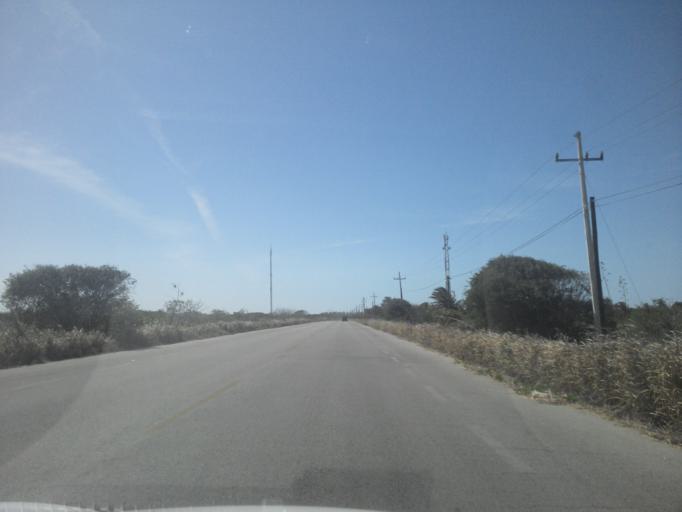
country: MX
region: Yucatan
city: Telchac Puerto
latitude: 21.3288
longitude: -89.3887
